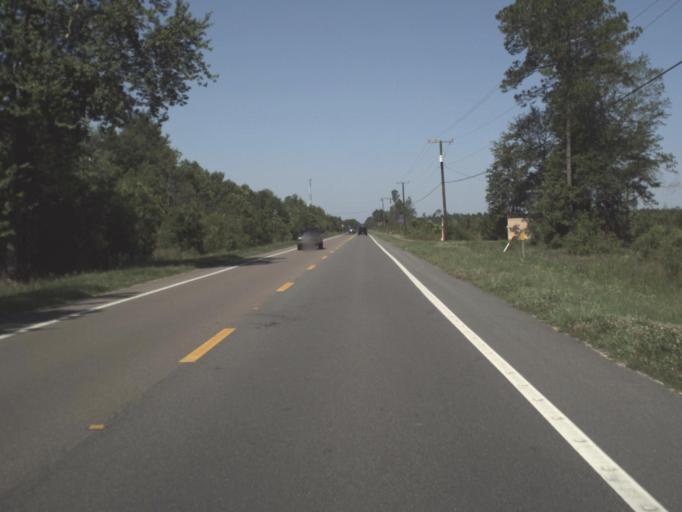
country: US
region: Florida
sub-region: Baker County
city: Macclenny
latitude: 30.2709
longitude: -82.1874
